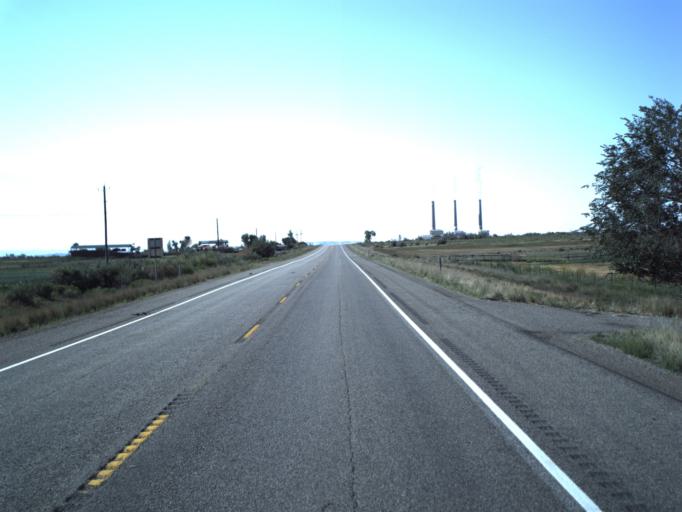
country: US
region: Utah
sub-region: Emery County
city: Castle Dale
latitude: 39.2038
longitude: -111.0243
